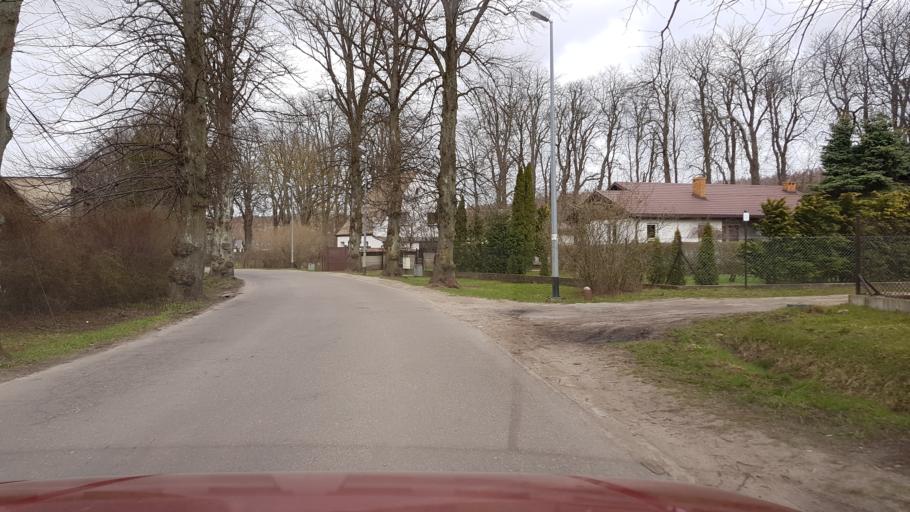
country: PL
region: West Pomeranian Voivodeship
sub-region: Powiat koszalinski
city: Sianow
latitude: 54.1854
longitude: 16.2436
